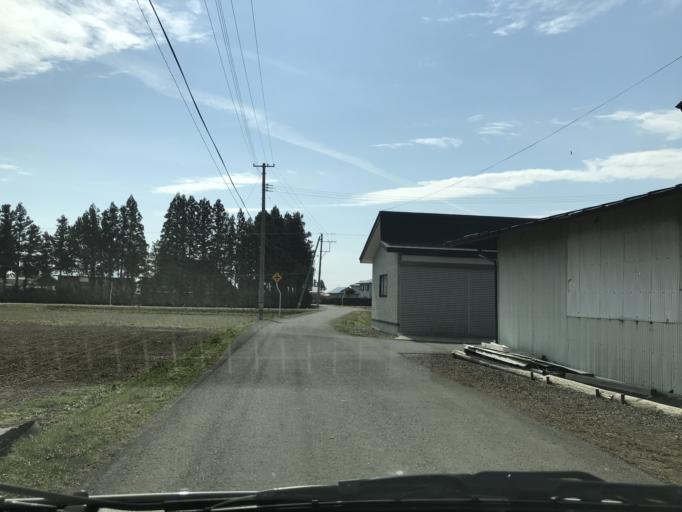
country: JP
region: Iwate
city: Mizusawa
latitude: 39.1383
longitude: 141.0556
